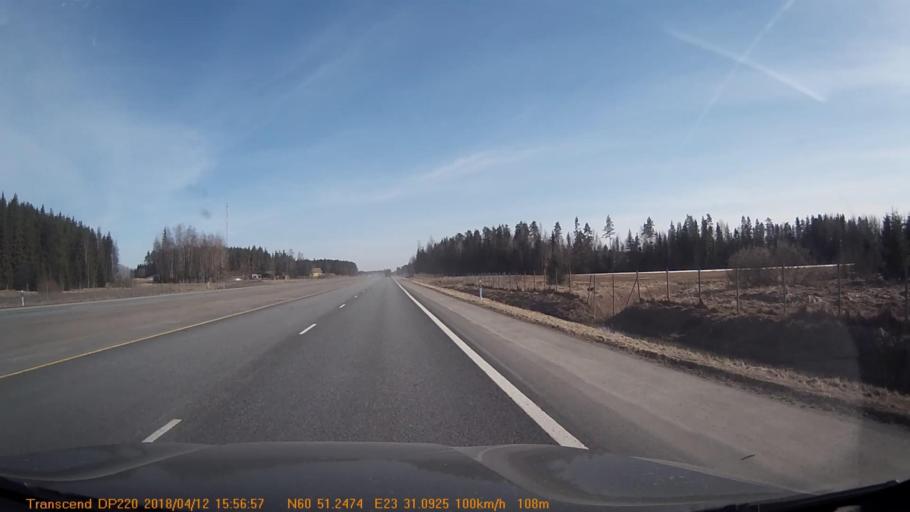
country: FI
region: Haeme
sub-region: Forssa
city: Jokioinen
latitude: 60.8540
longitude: 23.5184
